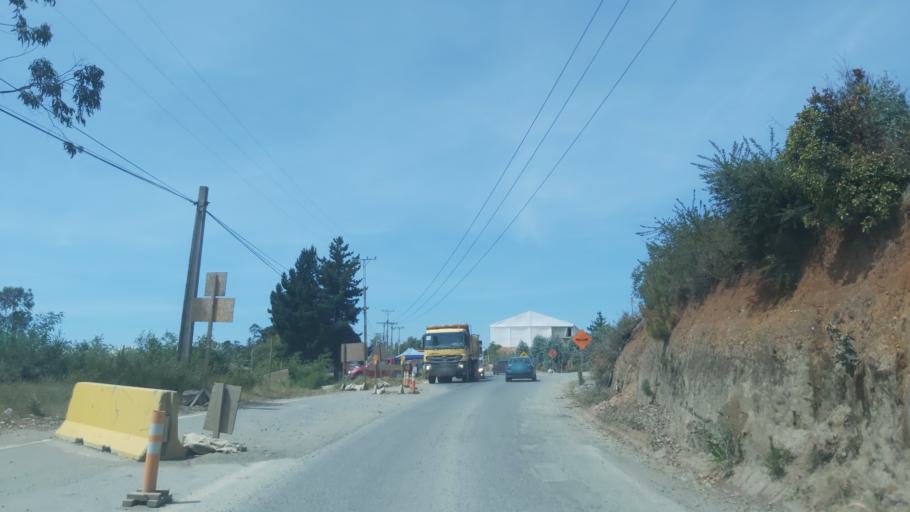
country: CL
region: Maule
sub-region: Provincia de Talca
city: Constitucion
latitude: -35.3758
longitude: -72.4210
